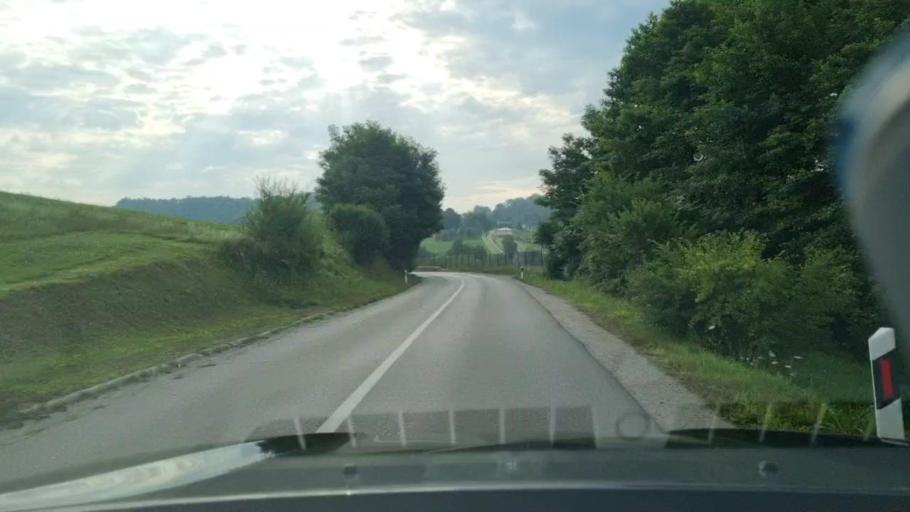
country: BA
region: Federation of Bosnia and Herzegovina
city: Podzvizd
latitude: 45.1711
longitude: 15.8490
